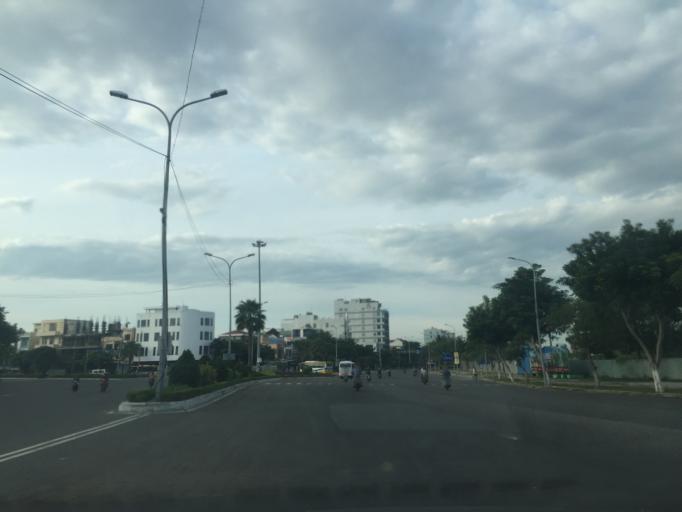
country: VN
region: Da Nang
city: Da Nang
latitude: 16.0887
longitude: 108.2151
